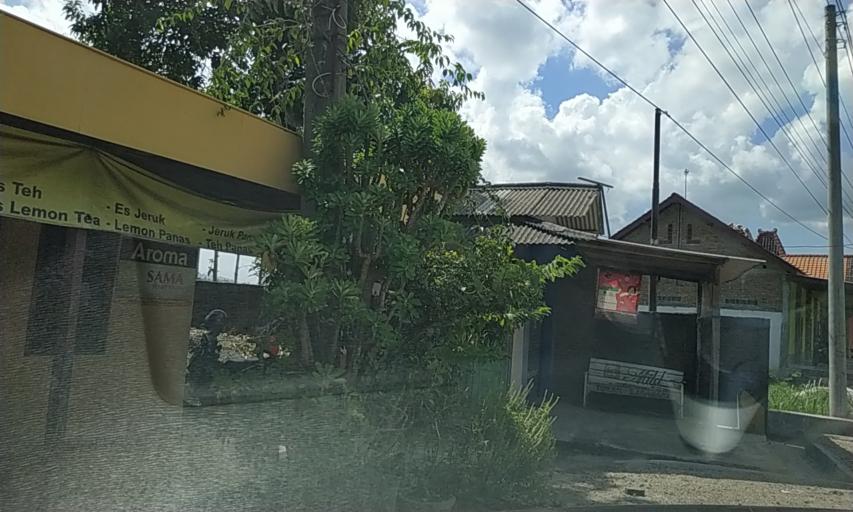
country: ID
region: East Java
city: Krajan
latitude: -8.0223
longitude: 110.8953
